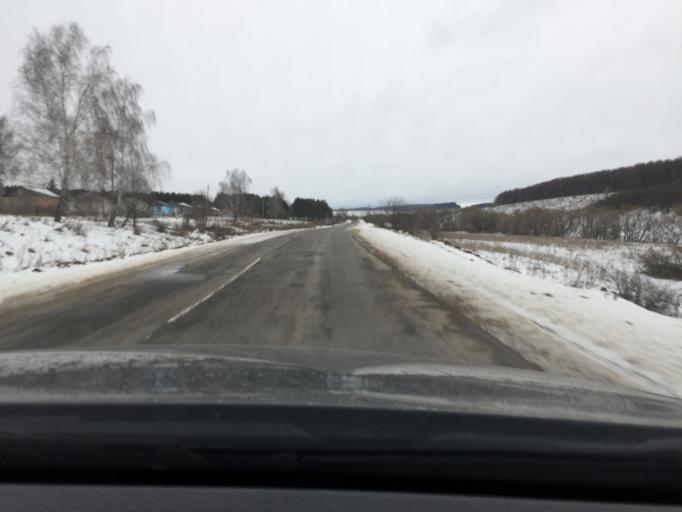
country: RU
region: Tula
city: Shchekino
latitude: 53.8256
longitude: 37.5587
